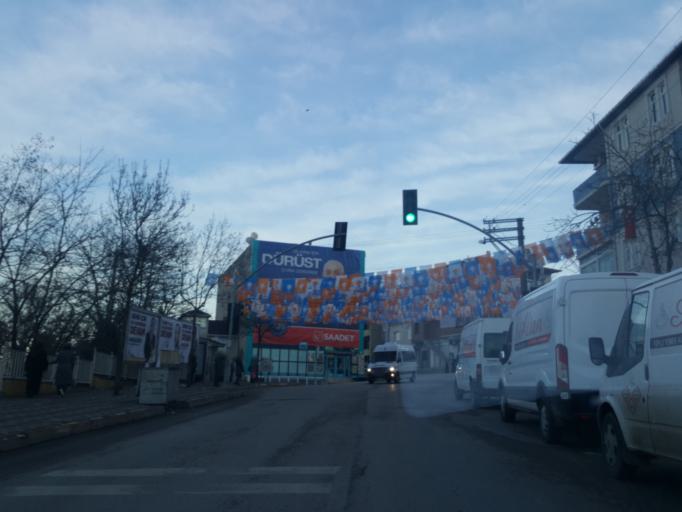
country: TR
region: Kocaeli
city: Tavsancil
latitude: 40.7889
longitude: 29.5387
